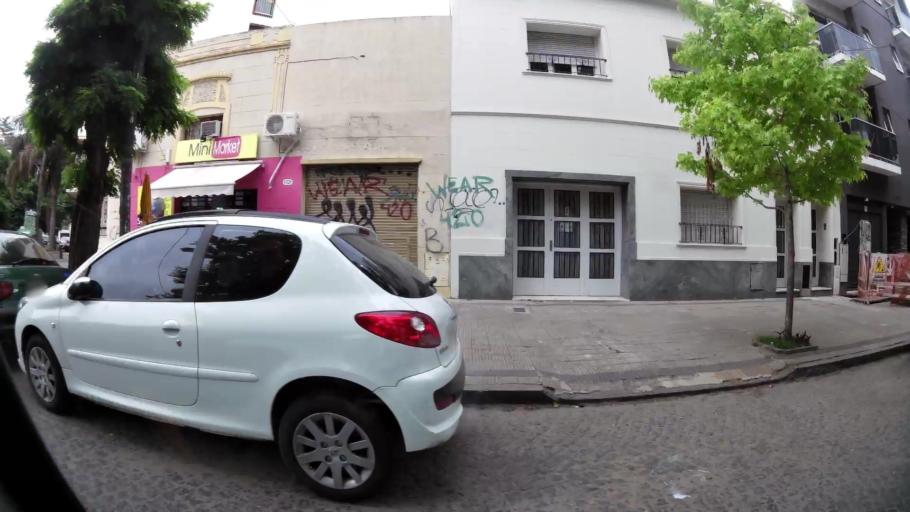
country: AR
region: Buenos Aires
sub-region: Partido de La Plata
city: La Plata
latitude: -34.9259
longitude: -57.9485
